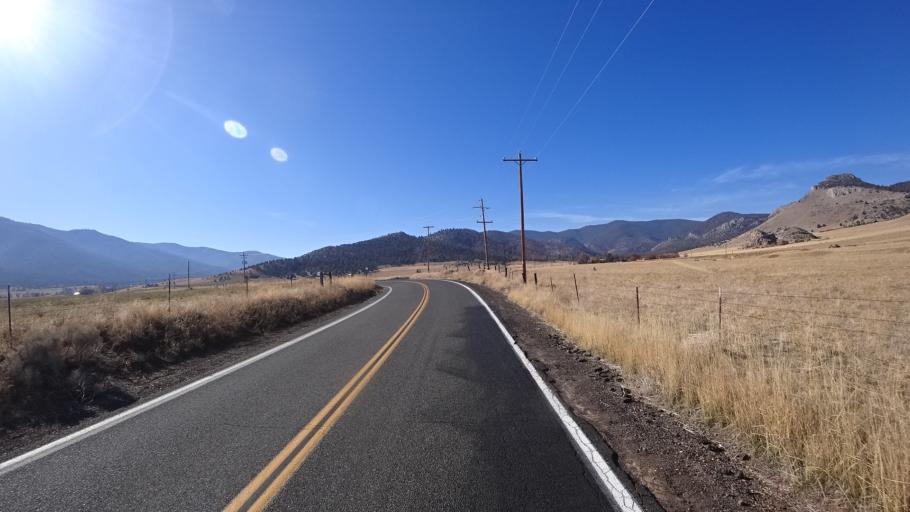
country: US
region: California
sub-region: Siskiyou County
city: Weed
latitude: 41.5039
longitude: -122.5487
